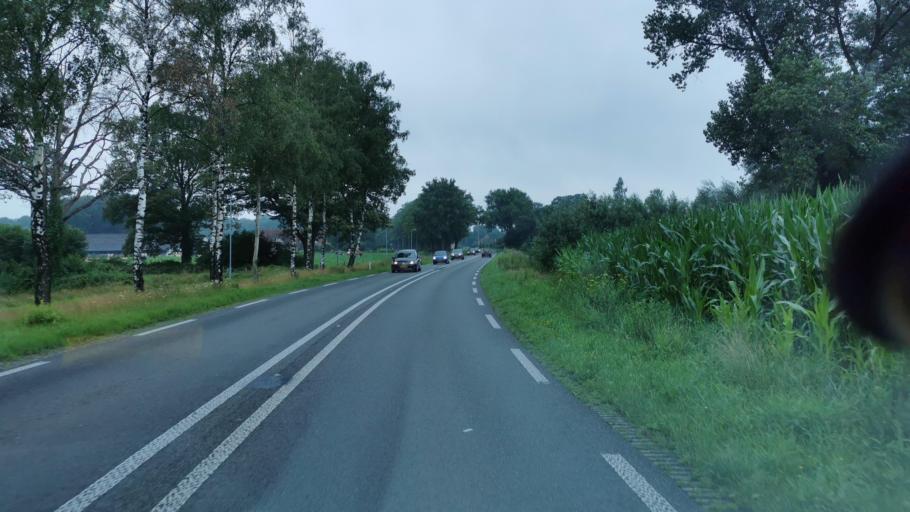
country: NL
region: Overijssel
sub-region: Gemeente Losser
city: Losser
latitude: 52.2730
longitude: 6.9813
